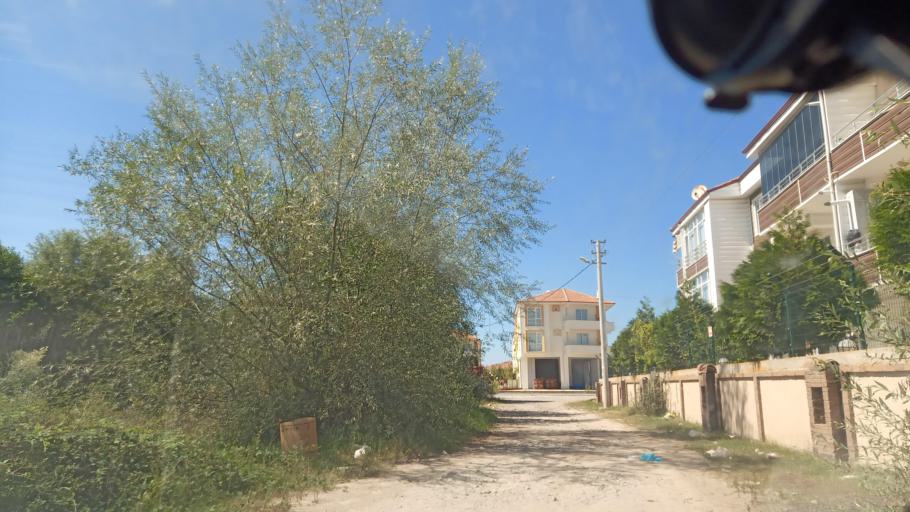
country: TR
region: Sakarya
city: Karasu
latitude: 41.1185
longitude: 30.6537
